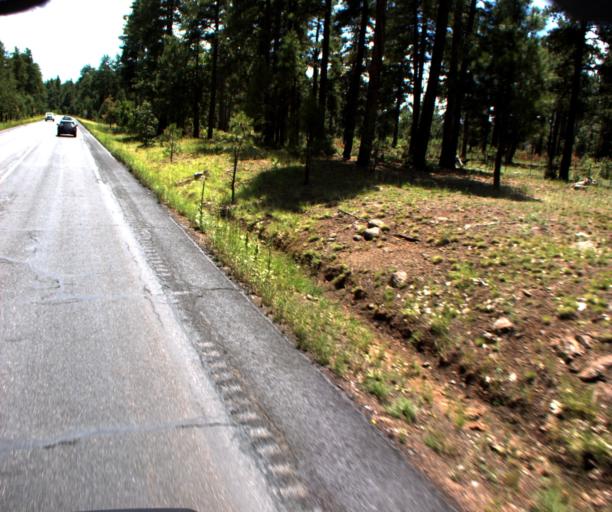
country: US
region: Arizona
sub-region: Gila County
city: Pine
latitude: 34.4703
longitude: -111.4487
